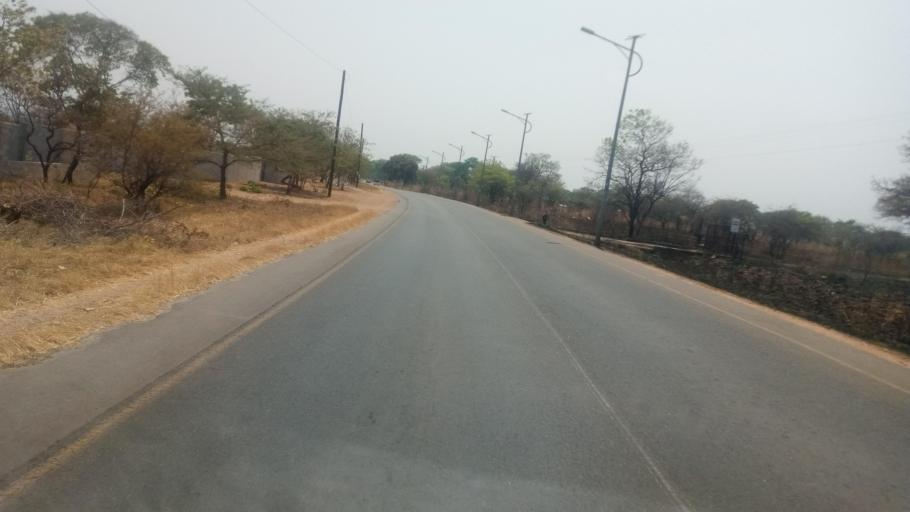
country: ZM
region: Lusaka
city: Lusaka
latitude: -15.4748
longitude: 28.4230
